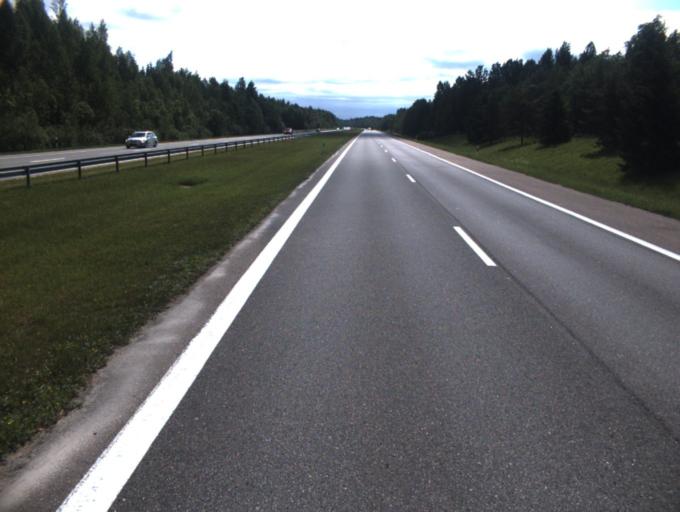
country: LT
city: Rietavas
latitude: 55.6560
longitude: 21.7799
